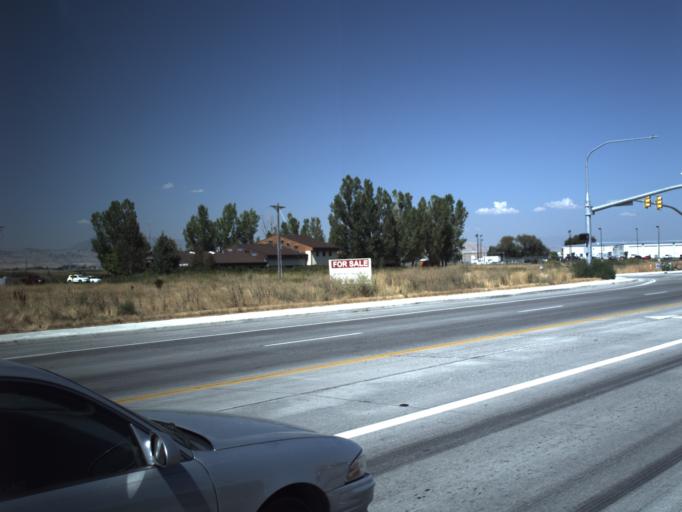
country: US
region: Utah
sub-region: Cache County
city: Logan
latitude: 41.7573
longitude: -111.8588
